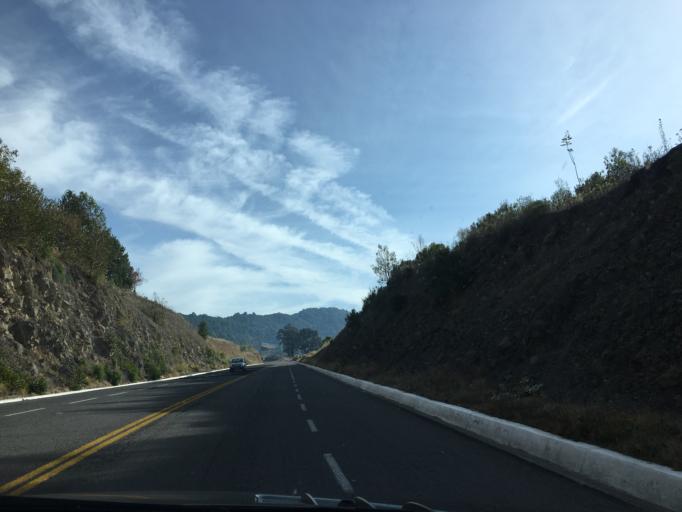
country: MX
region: Mexico
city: San Bartolo
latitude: 19.2706
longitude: -100.0603
